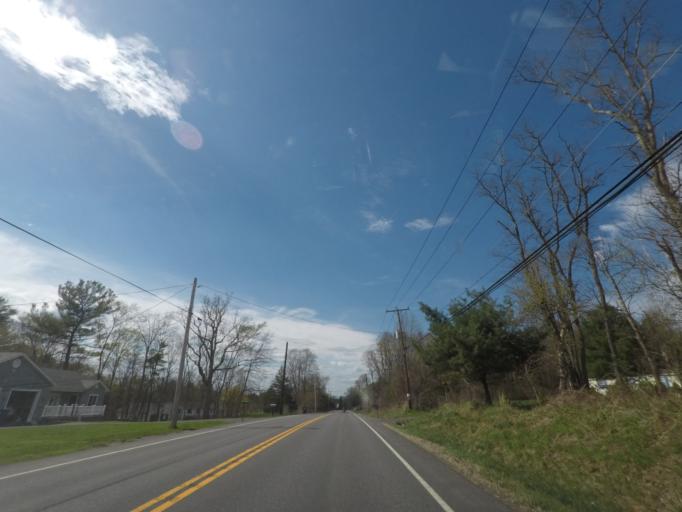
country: US
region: New York
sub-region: Greene County
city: Cairo
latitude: 42.3409
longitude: -74.0281
